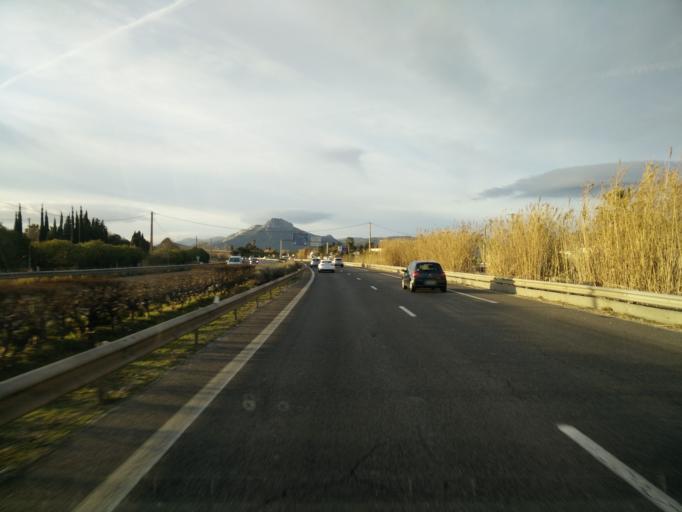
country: FR
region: Provence-Alpes-Cote d'Azur
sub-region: Departement du Var
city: La Crau
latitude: 43.1235
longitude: 6.0962
